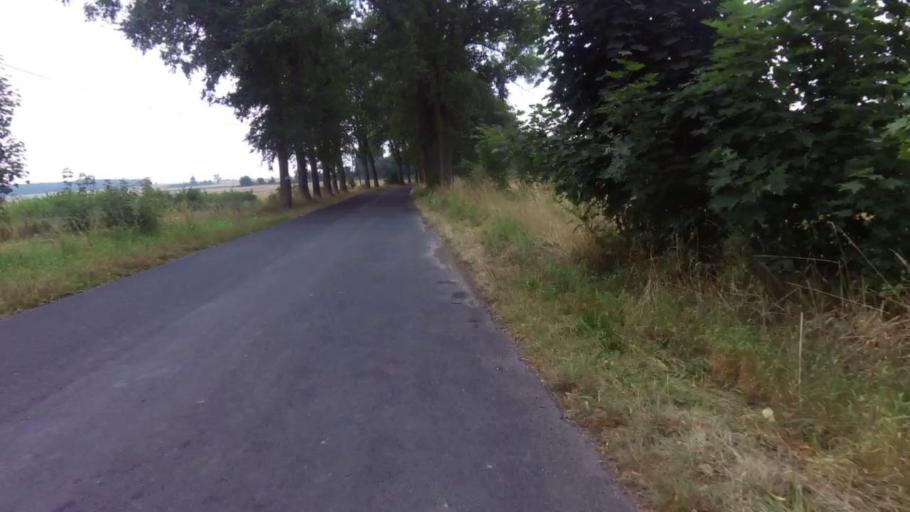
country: PL
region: West Pomeranian Voivodeship
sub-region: Powiat choszczenski
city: Choszczno
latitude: 53.2088
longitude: 15.3926
